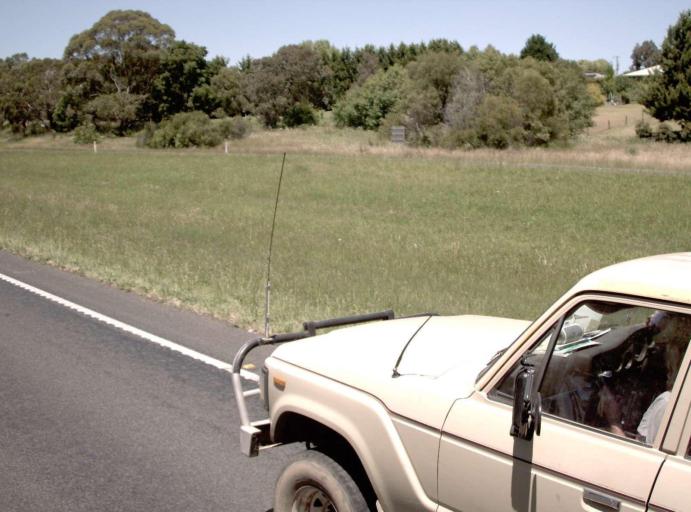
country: AU
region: Victoria
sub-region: Baw Baw
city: Warragul
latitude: -38.1025
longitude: 145.8541
